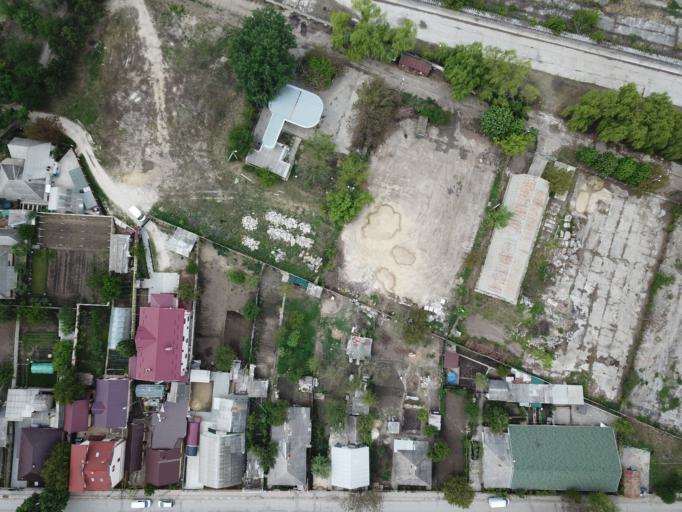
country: MD
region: Ungheni
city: Ungheni
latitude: 47.2189
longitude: 27.8033
